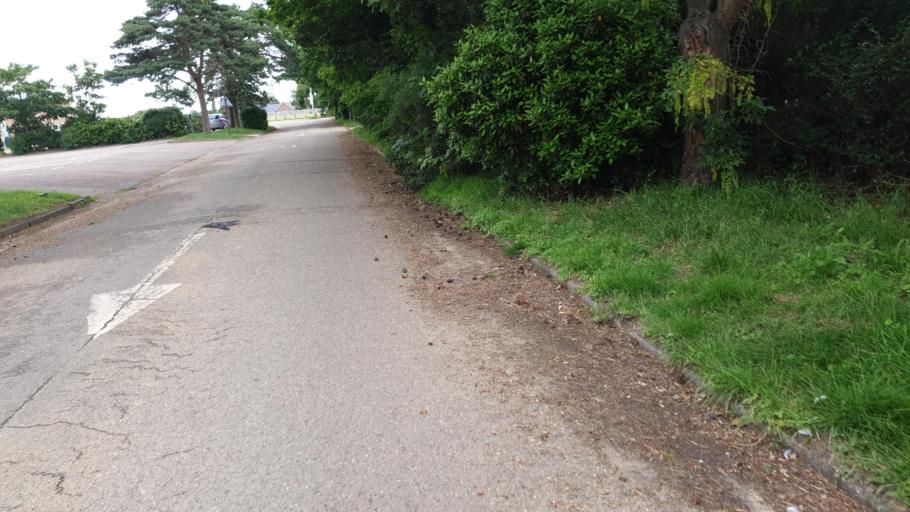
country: GB
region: England
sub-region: Essex
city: Clacton-on-Sea
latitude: 51.7971
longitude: 1.1603
